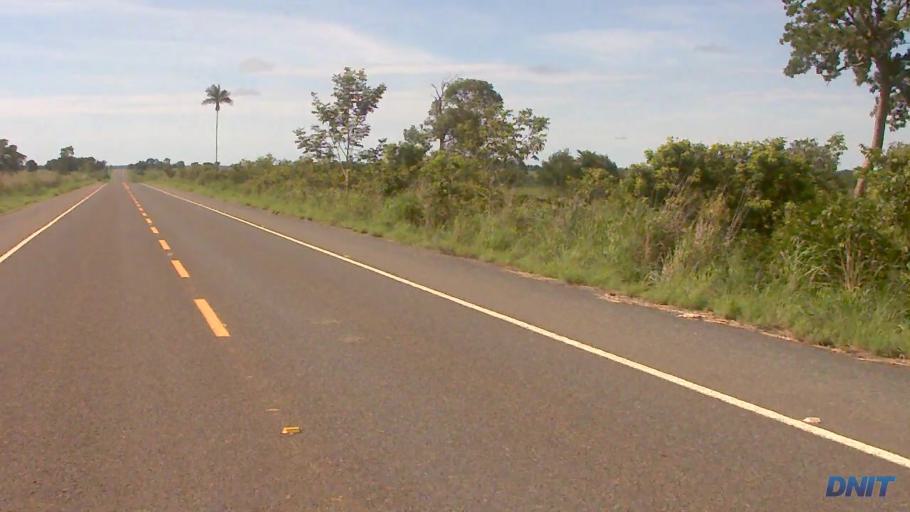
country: BR
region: Goias
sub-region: Sao Miguel Do Araguaia
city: Sao Miguel do Araguaia
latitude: -13.4441
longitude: -50.1225
